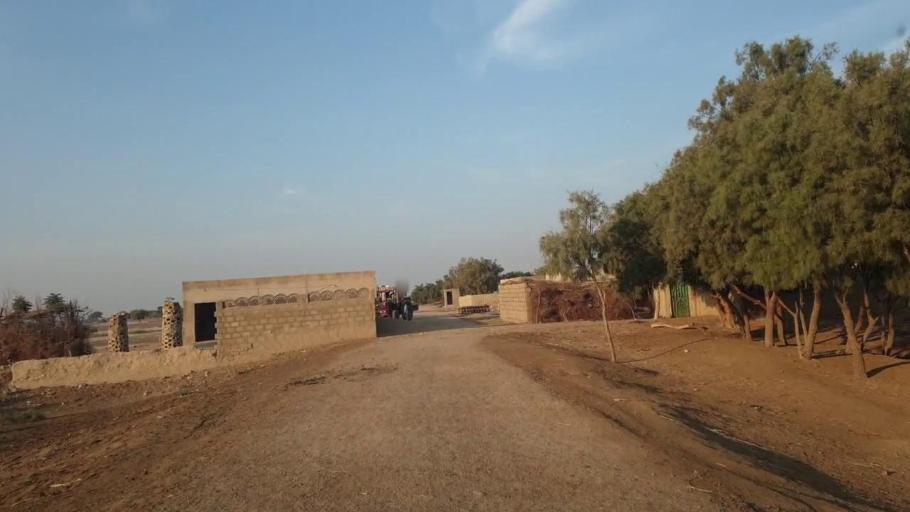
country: PK
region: Sindh
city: Sann
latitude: 25.9229
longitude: 68.1921
